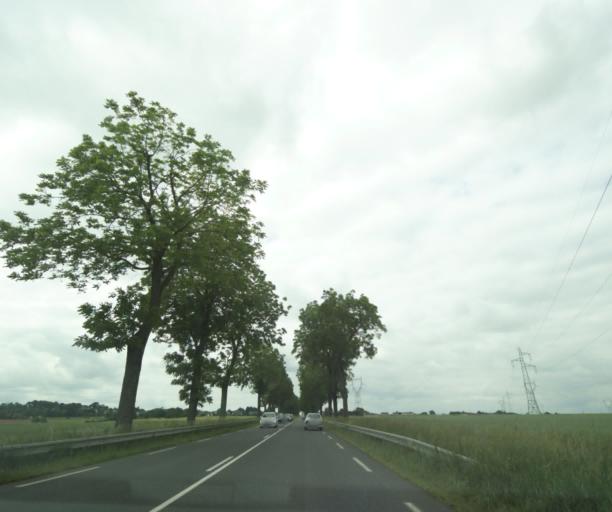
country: FR
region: Pays de la Loire
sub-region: Departement de Maine-et-Loire
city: Distre
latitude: 47.2042
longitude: -0.1211
